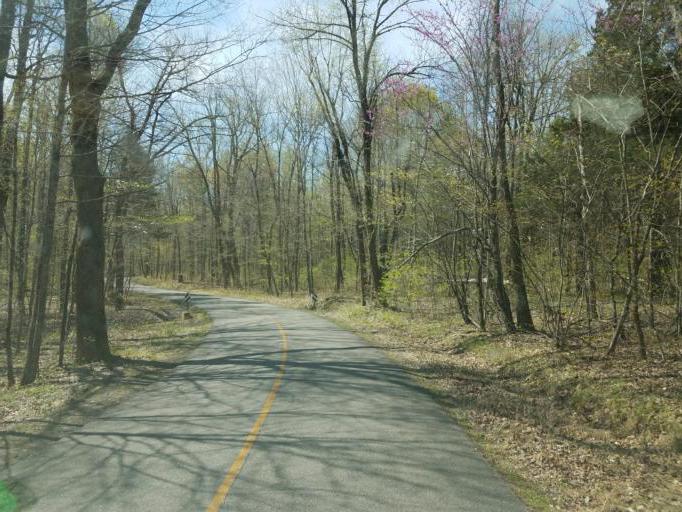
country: US
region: Kentucky
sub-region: Barren County
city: Cave City
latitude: 37.1589
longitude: -86.0454
